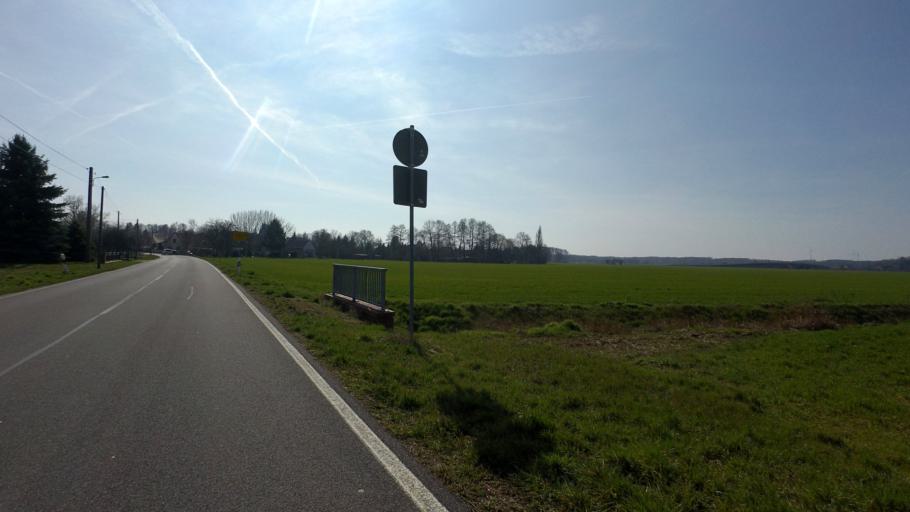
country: DE
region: Brandenburg
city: Drahnsdorf
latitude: 51.9419
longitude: 13.5980
